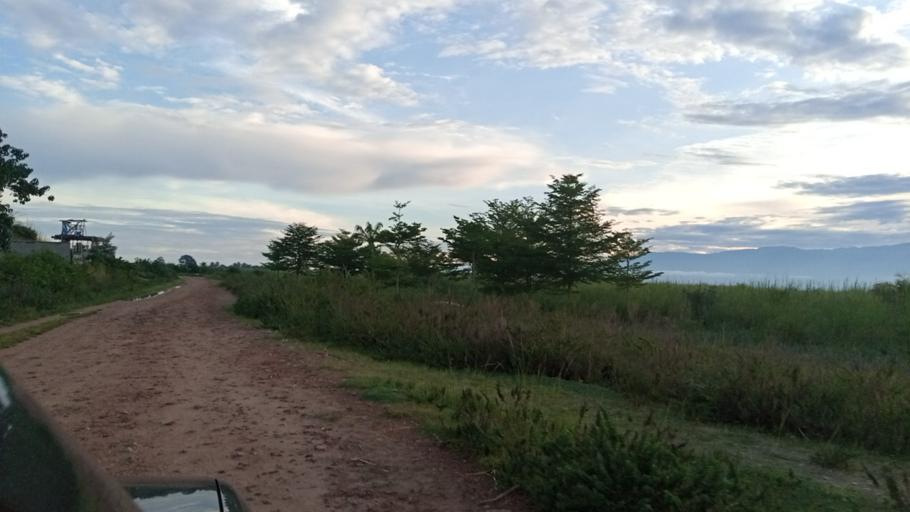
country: BI
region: Bujumbura Mairie
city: Bujumbura
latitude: -3.4627
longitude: 29.3429
